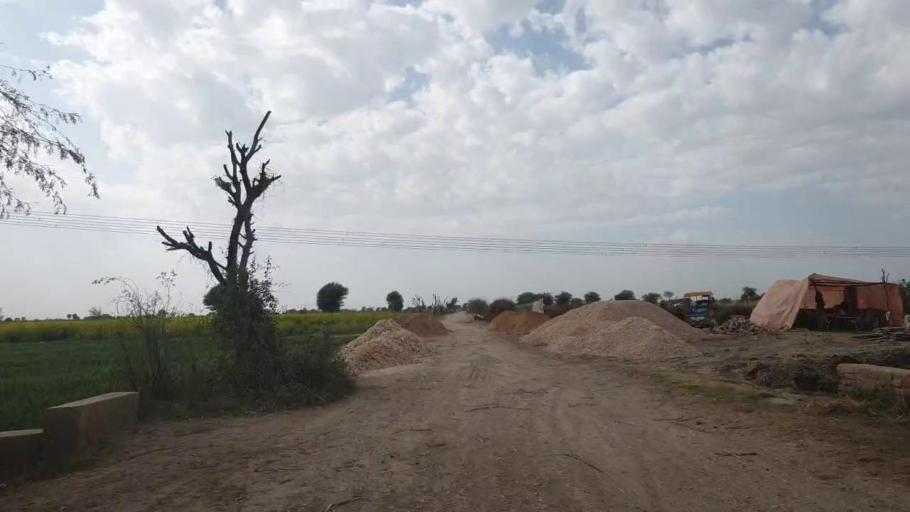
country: PK
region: Sindh
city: Hala
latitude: 25.9343
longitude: 68.4505
